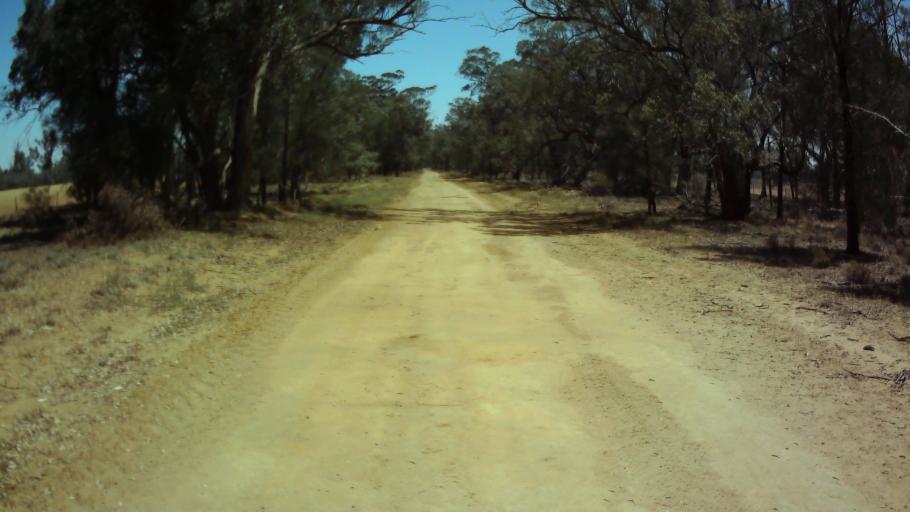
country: AU
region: New South Wales
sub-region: Weddin
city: Grenfell
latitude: -34.0423
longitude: 147.8445
